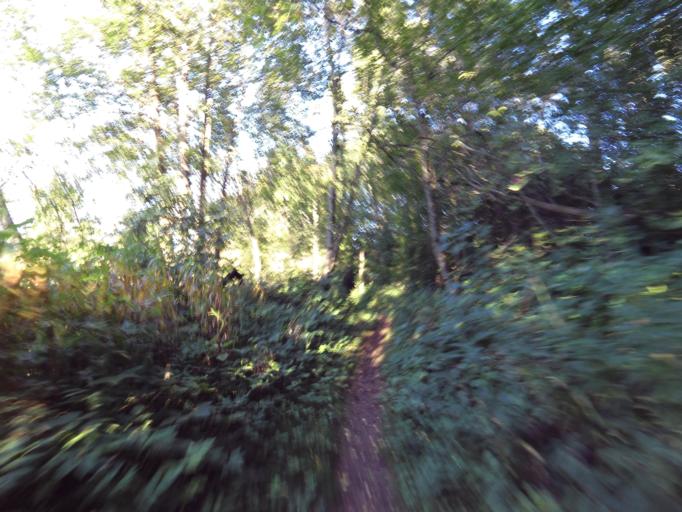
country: SE
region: Gaevleborg
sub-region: Gavle Kommun
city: Gavle
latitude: 60.7164
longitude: 17.1477
